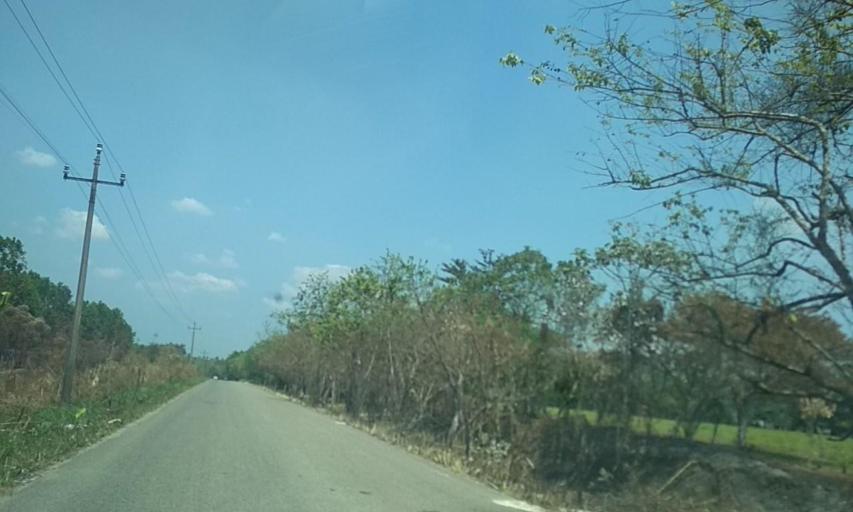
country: MX
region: Tabasco
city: Huimanguillo
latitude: 17.8001
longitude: -93.4647
